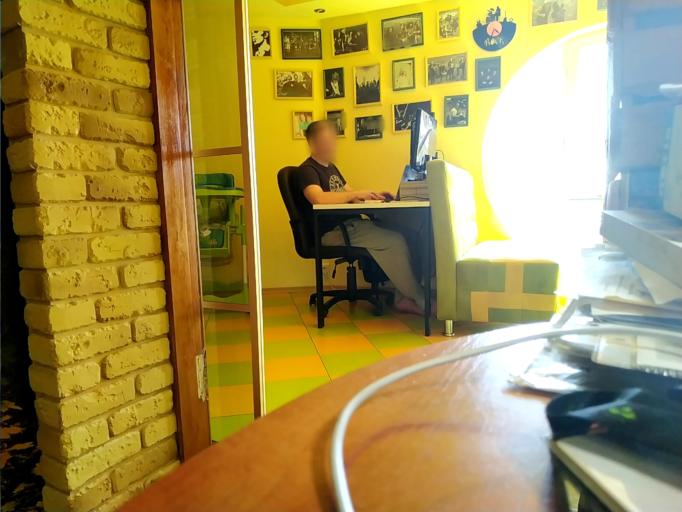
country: RU
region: Moskovskaya
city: Pavlovskiy Posad
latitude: 55.7464
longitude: 38.7074
